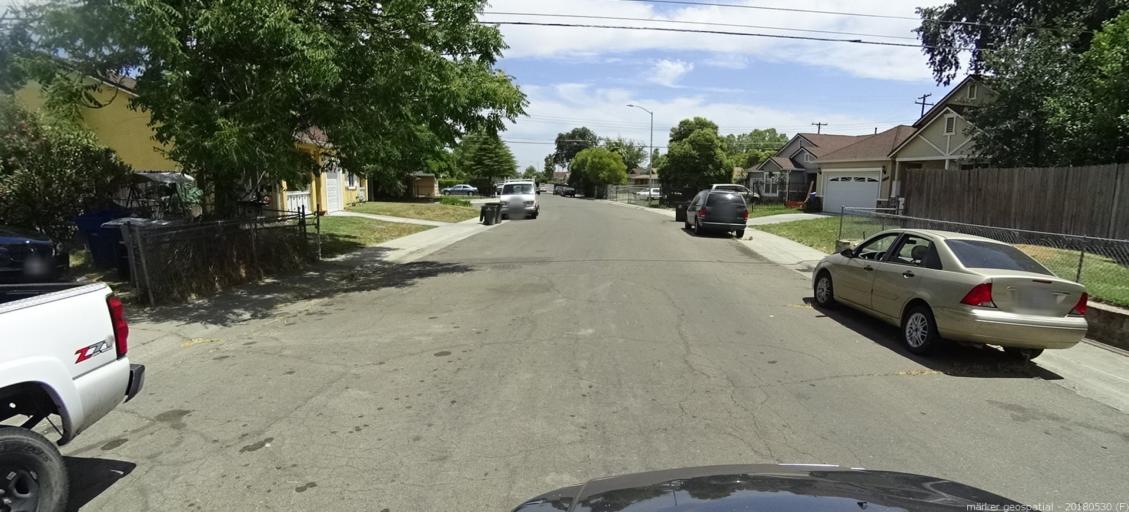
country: US
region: California
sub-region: Sacramento County
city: Sacramento
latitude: 38.6274
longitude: -121.4659
